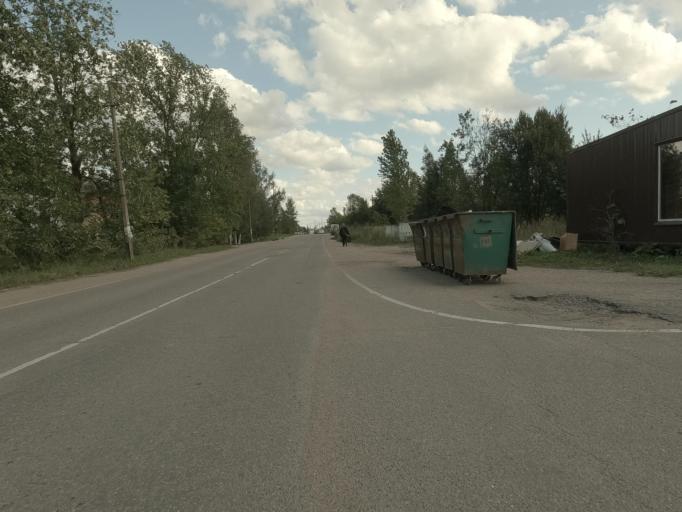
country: RU
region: Leningrad
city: Ul'yanovka
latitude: 59.6358
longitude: 30.7583
